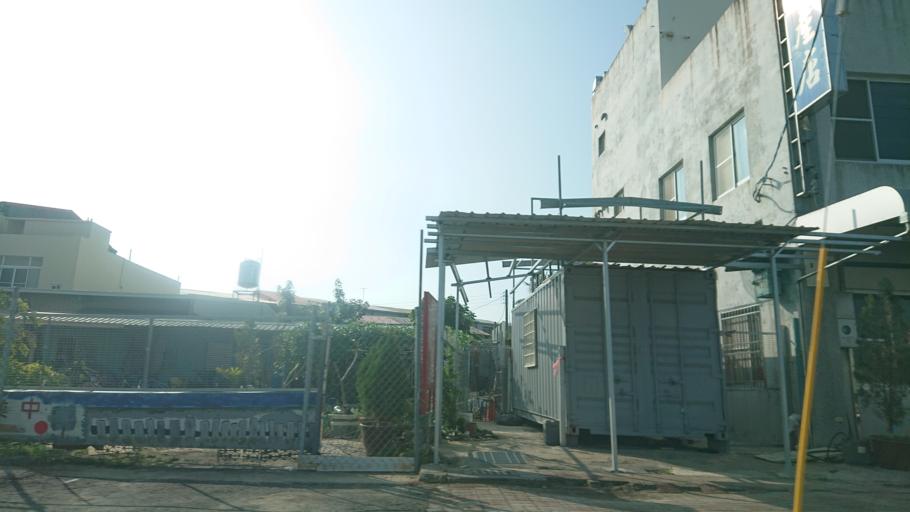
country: TW
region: Taiwan
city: Xinying
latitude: 23.3338
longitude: 120.2504
